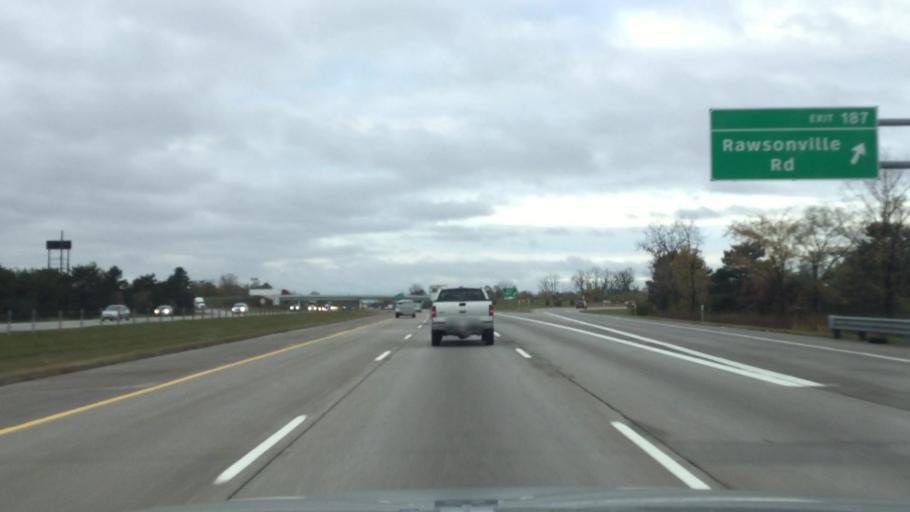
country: US
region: Michigan
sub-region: Wayne County
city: Belleville
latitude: 42.2189
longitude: -83.5396
